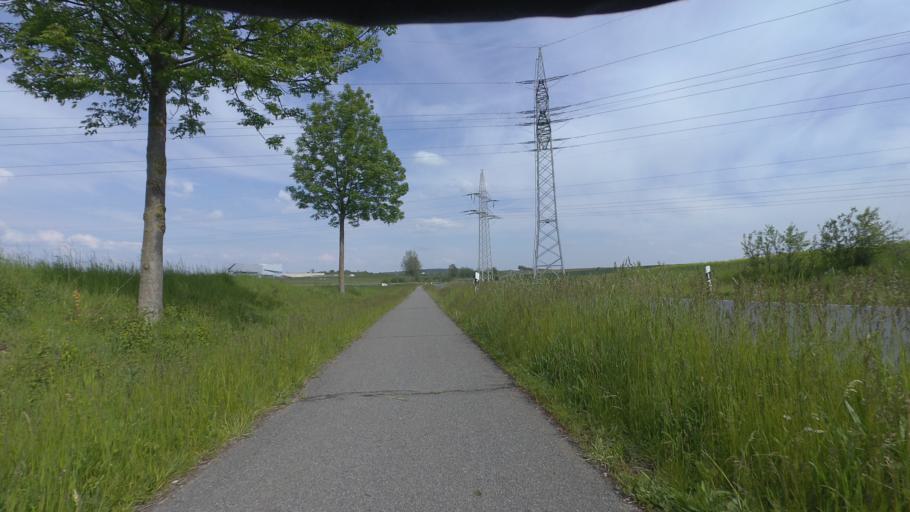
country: DE
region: Lower Saxony
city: Schoningen
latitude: 52.1289
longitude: 10.9842
